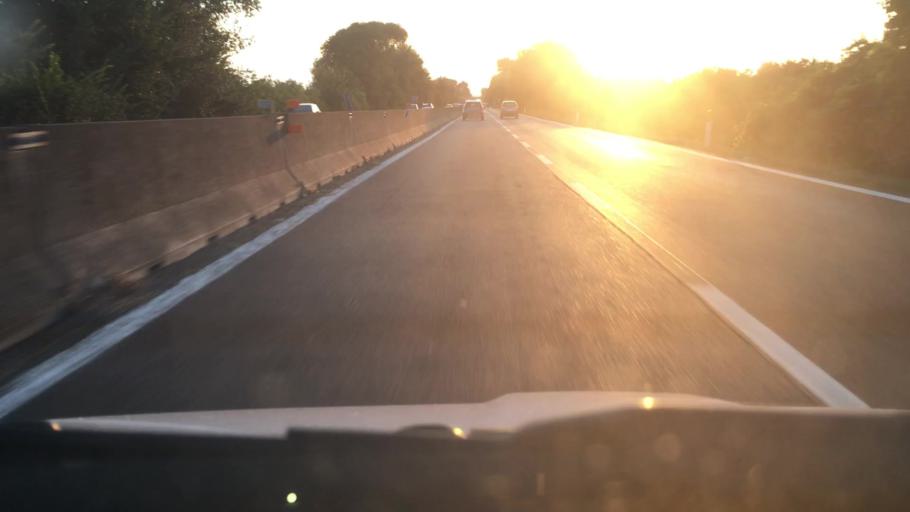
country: IT
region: Emilia-Romagna
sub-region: Provincia di Ferrara
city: Masi-Torello
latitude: 44.7795
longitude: 11.7795
